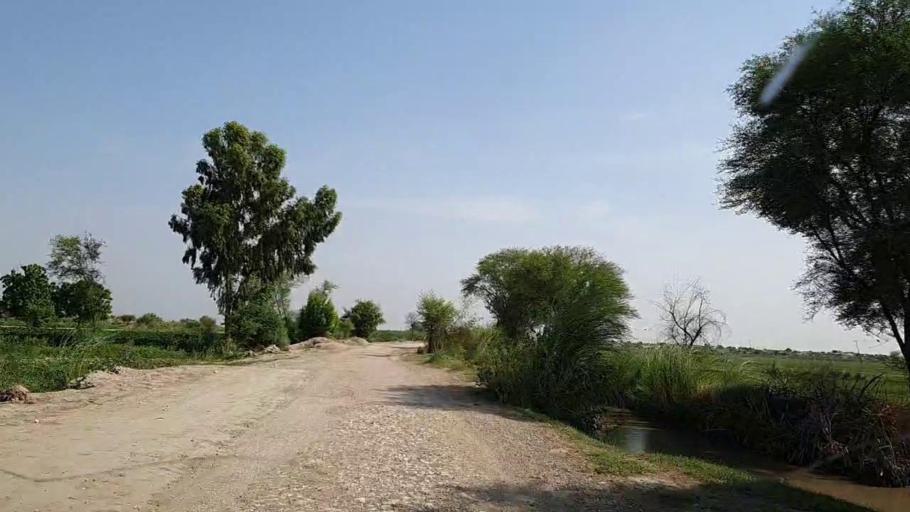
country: PK
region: Sindh
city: Khanpur
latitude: 27.7208
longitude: 69.3607
